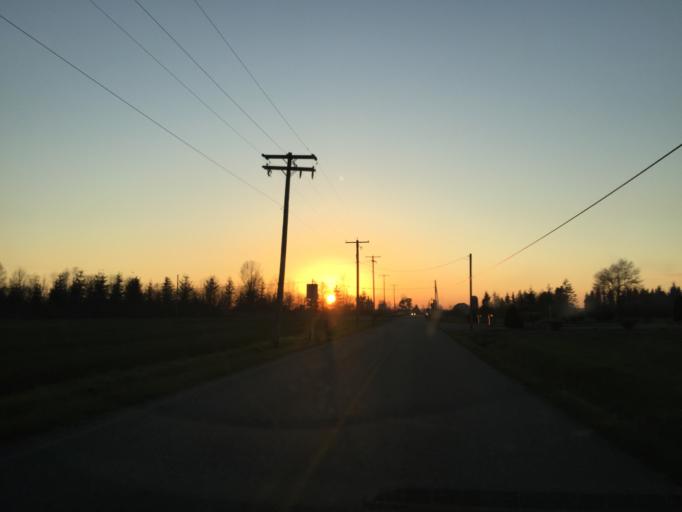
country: US
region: Washington
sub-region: Whatcom County
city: Sumas
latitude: 48.9819
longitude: -122.2362
